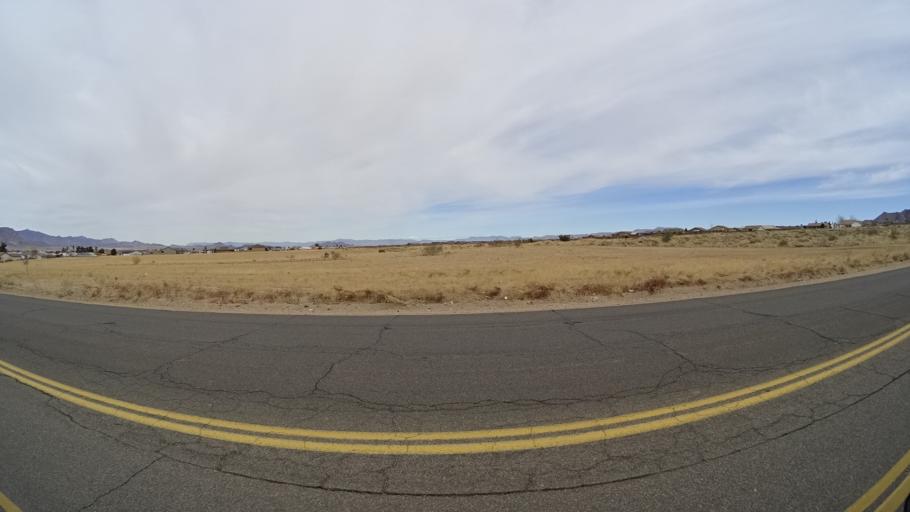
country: US
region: Arizona
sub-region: Mohave County
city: Kingman
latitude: 35.1854
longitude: -114.0053
